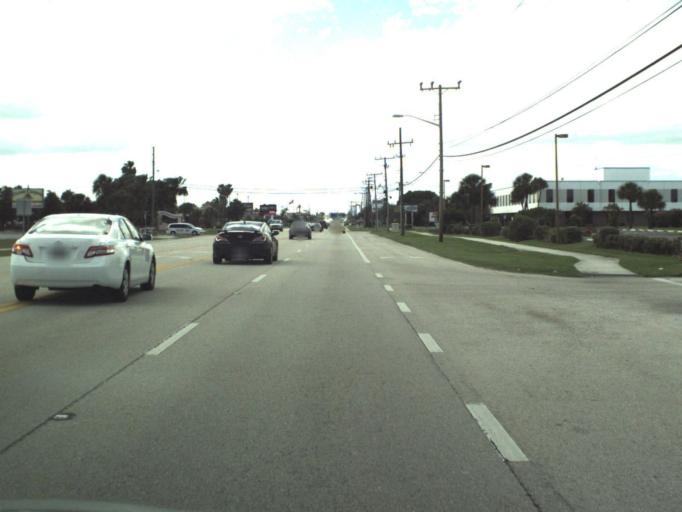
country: US
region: Florida
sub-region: Brevard County
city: Cape Canaveral
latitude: 28.3932
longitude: -80.6094
